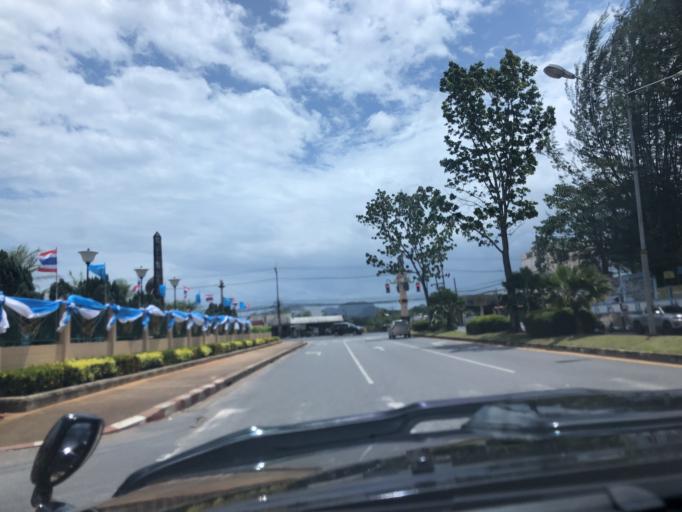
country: TH
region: Krabi
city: Krabi
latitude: 8.0854
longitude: 98.9072
